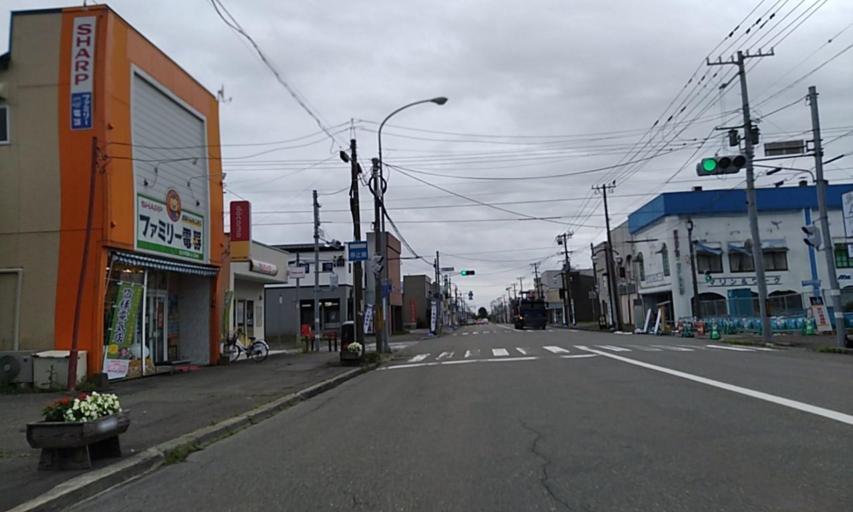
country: JP
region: Hokkaido
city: Obihiro
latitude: 42.2890
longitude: 143.3152
